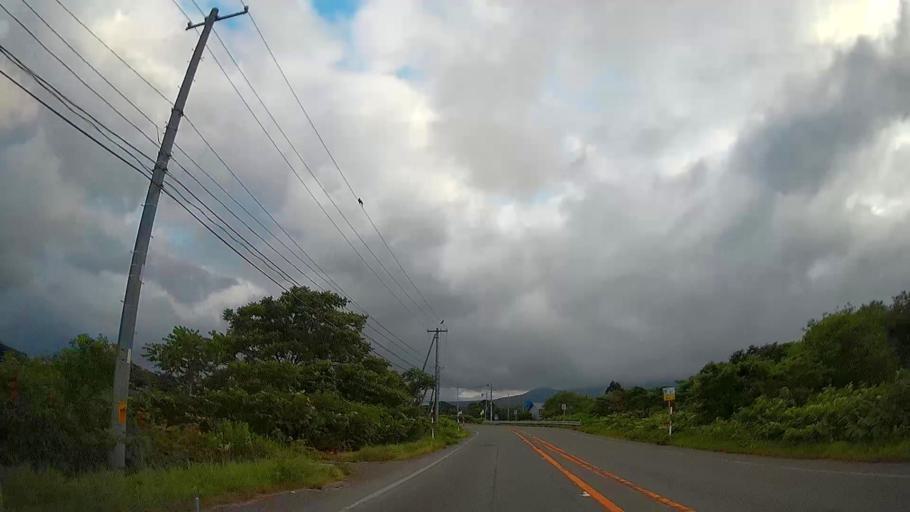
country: JP
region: Hokkaido
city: Nanae
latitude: 42.1106
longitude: 140.7572
